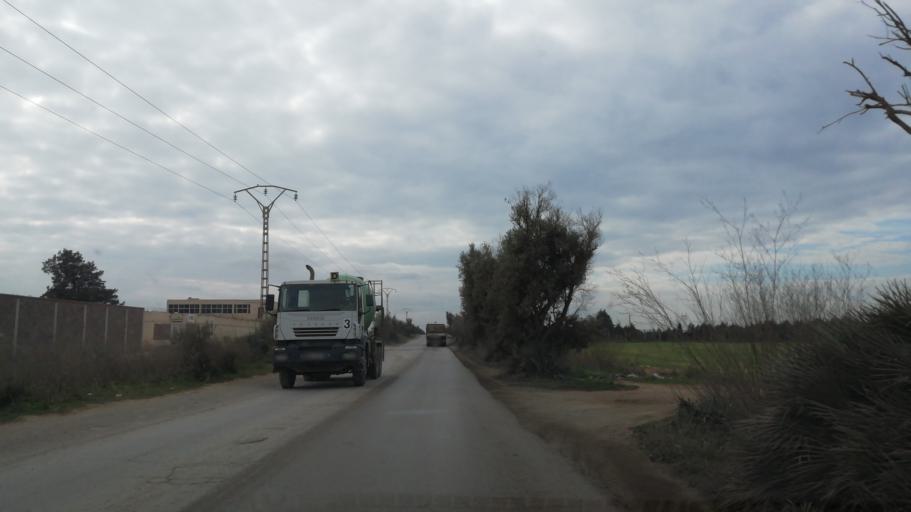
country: DZ
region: Oran
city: Ain el Bya
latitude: 35.7812
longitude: -0.3446
